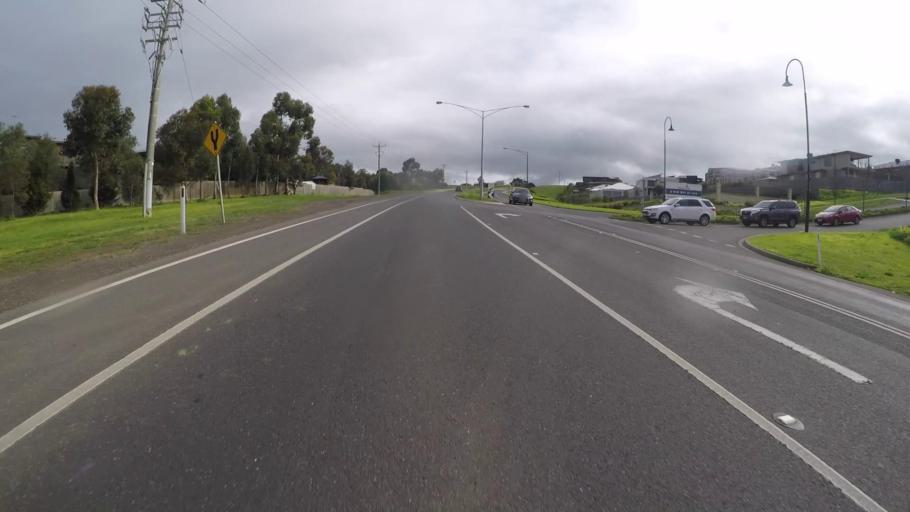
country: AU
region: Victoria
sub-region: Greater Geelong
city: Wandana Heights
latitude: -38.1708
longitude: 144.3011
